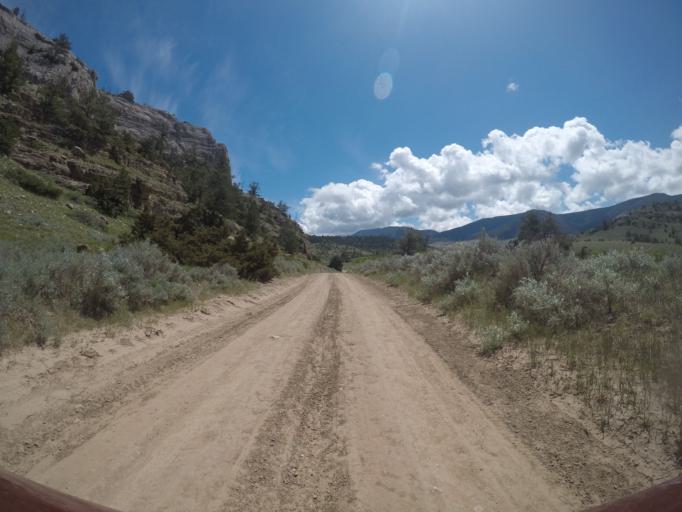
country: US
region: Wyoming
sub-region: Big Horn County
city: Lovell
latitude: 45.2239
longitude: -108.5956
